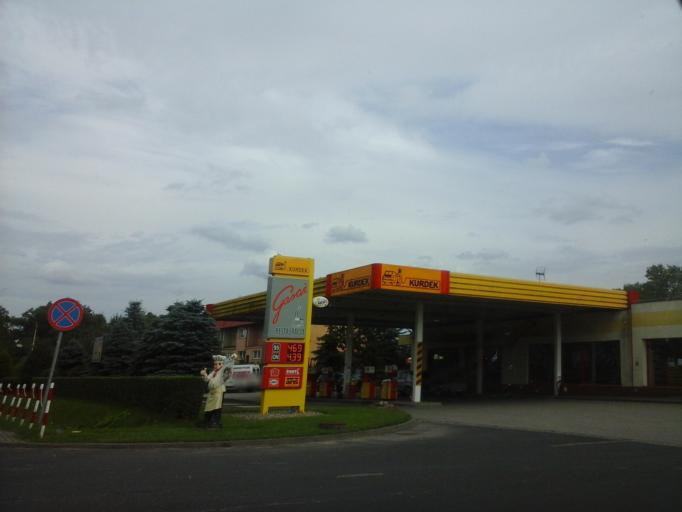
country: PL
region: West Pomeranian Voivodeship
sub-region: Powiat stargardzki
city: Suchan
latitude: 53.2769
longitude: 15.3375
